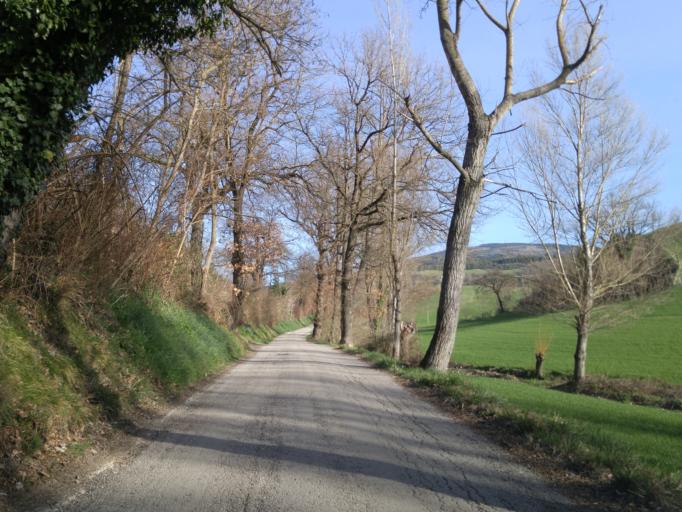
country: IT
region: The Marches
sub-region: Provincia di Pesaro e Urbino
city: Fermignano
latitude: 43.6794
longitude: 12.6560
